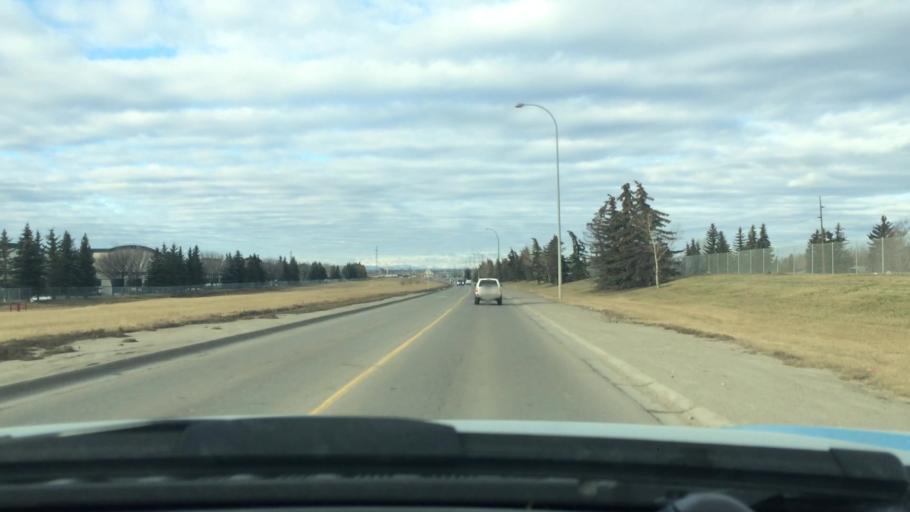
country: CA
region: Alberta
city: Calgary
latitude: 51.0154
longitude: -113.9861
